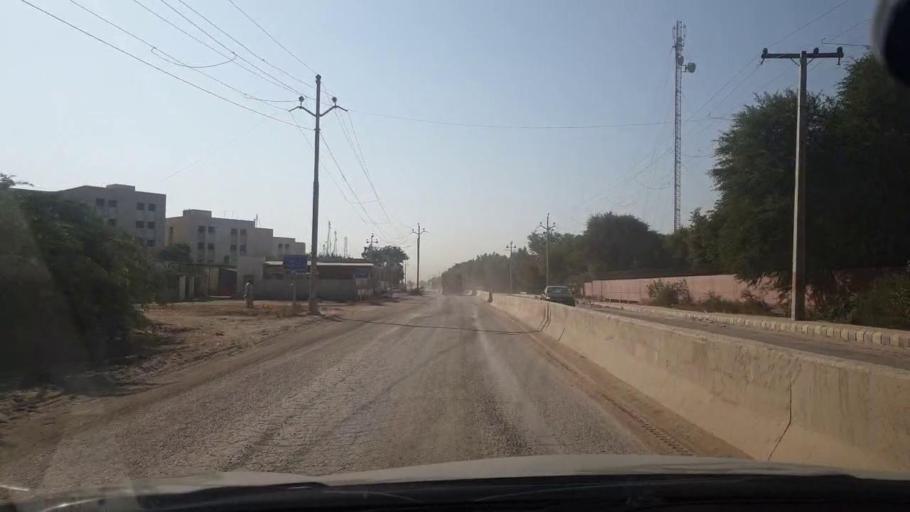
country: PK
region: Sindh
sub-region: Karachi District
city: Karachi
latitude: 25.0850
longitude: 67.0126
